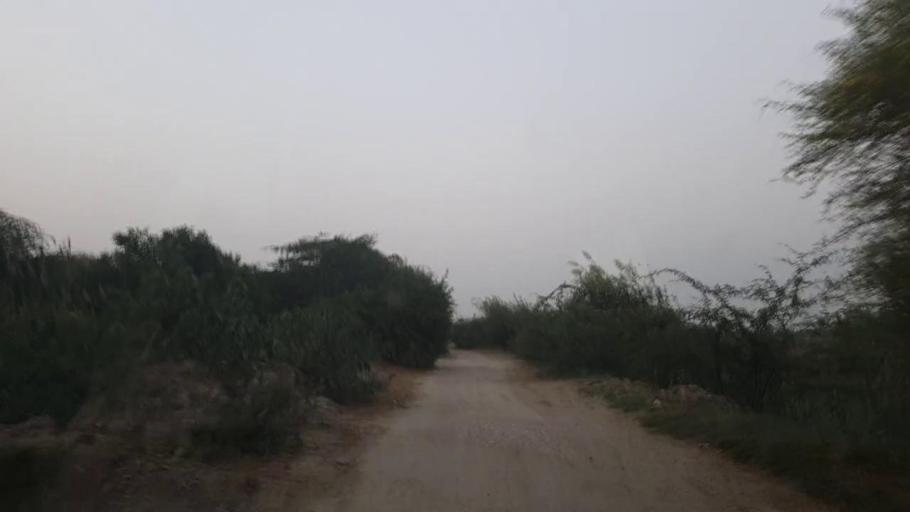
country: PK
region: Sindh
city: Mirpur Sakro
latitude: 24.5842
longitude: 67.7844
